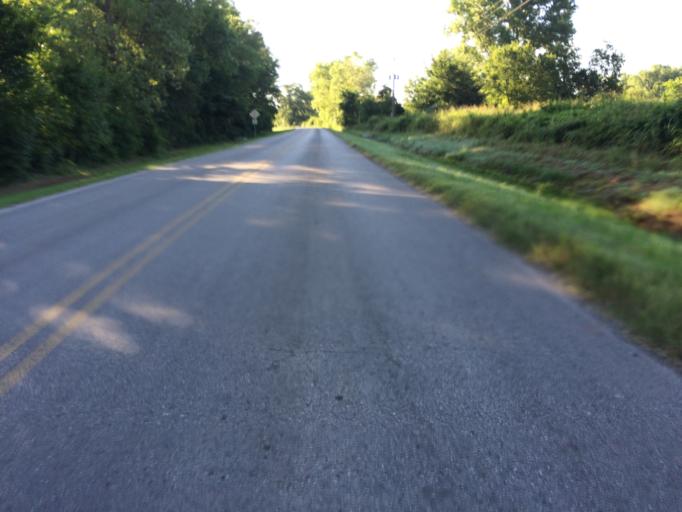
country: US
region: Oklahoma
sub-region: McClain County
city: Goldsby
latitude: 35.1747
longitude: -97.4497
